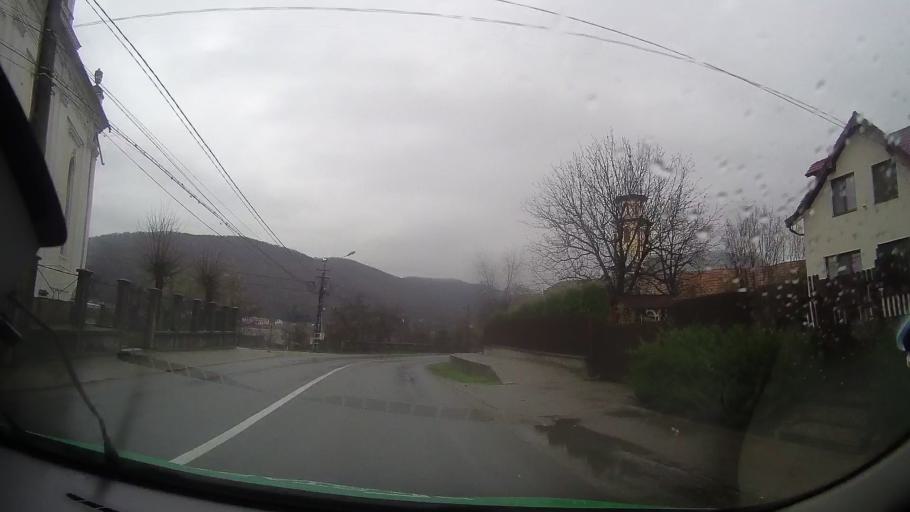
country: RO
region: Bistrita-Nasaud
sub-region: Municipiul Bistrita
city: Viisoara
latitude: 47.0723
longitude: 24.4355
